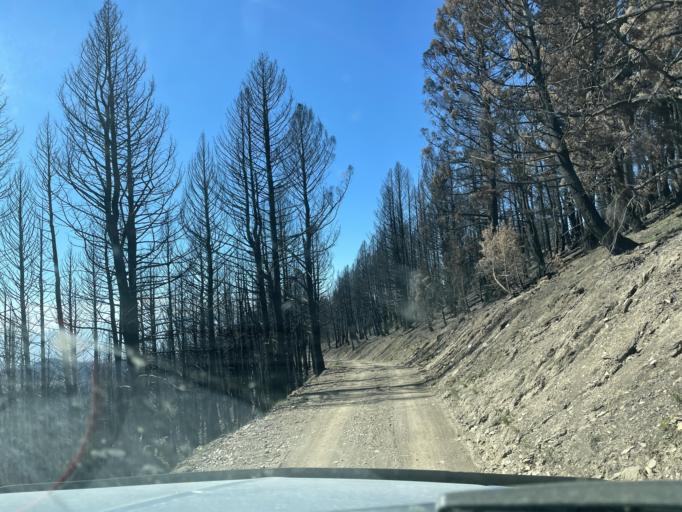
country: US
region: Montana
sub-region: Broadwater County
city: Townsend
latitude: 46.5073
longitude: -111.2781
